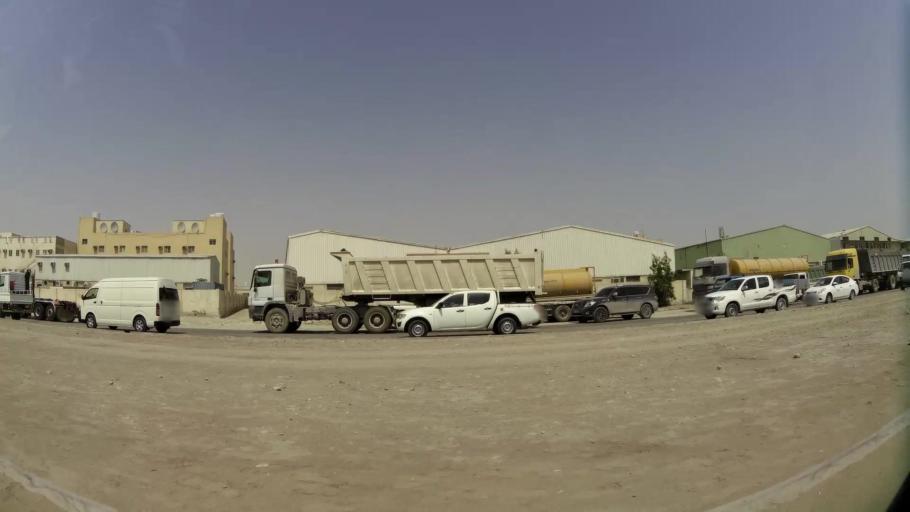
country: QA
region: Baladiyat ar Rayyan
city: Ar Rayyan
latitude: 25.1835
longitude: 51.4268
